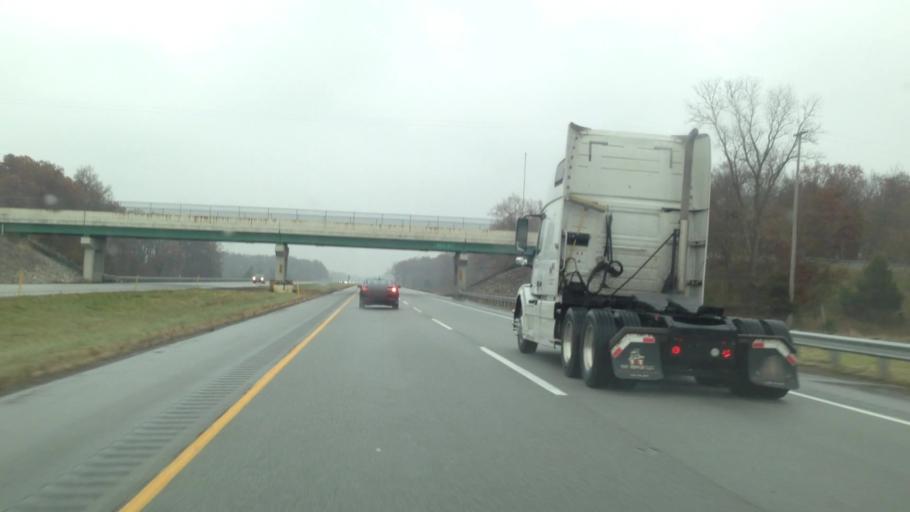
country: US
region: Indiana
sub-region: Saint Joseph County
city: Granger
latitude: 41.7312
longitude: -86.0826
